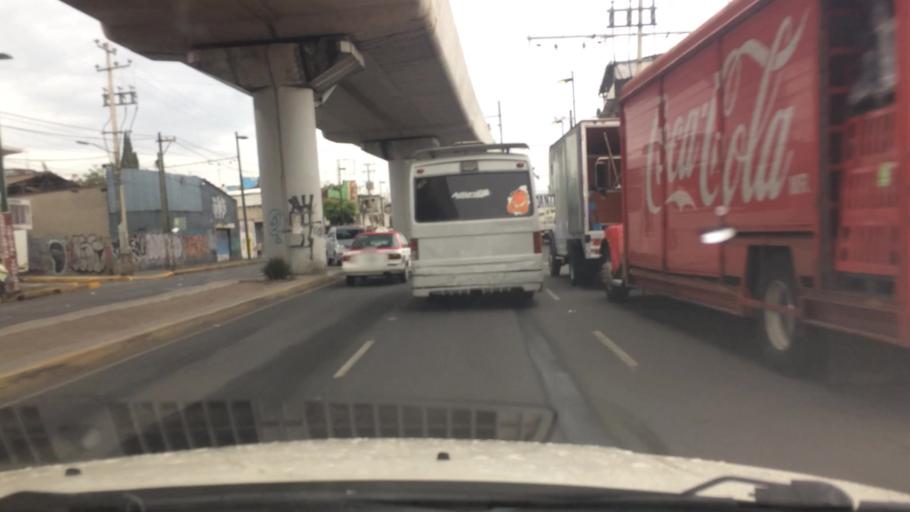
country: MX
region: Mexico City
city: Iztapalapa
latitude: 19.3319
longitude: -99.1079
